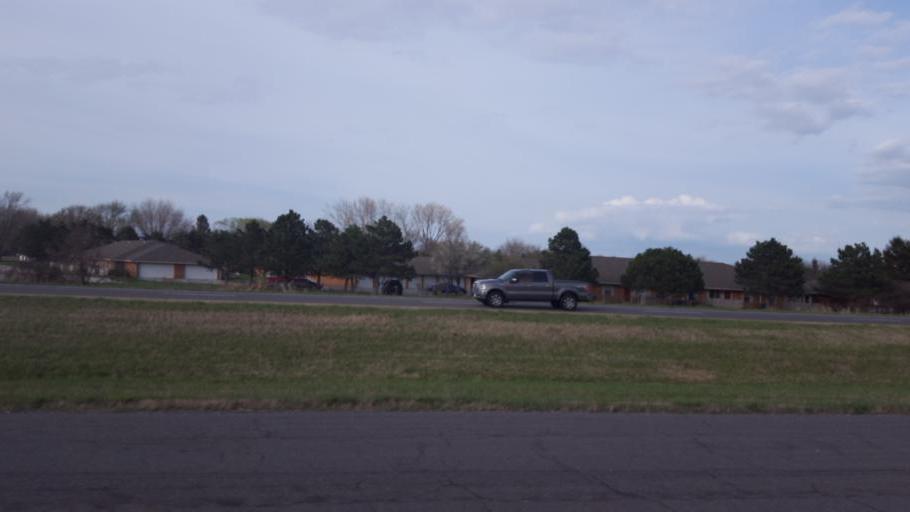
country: US
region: Ohio
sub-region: Erie County
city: Sandusky
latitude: 41.4466
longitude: -82.7867
